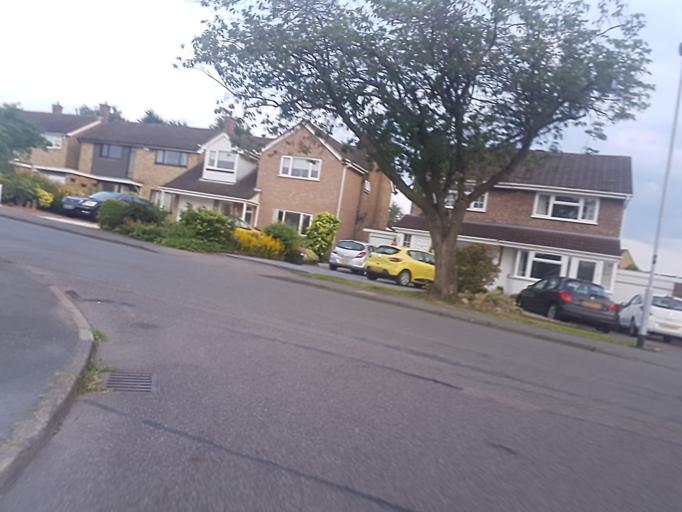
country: GB
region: England
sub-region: Leicestershire
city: Hinckley
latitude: 52.5519
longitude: -1.3607
